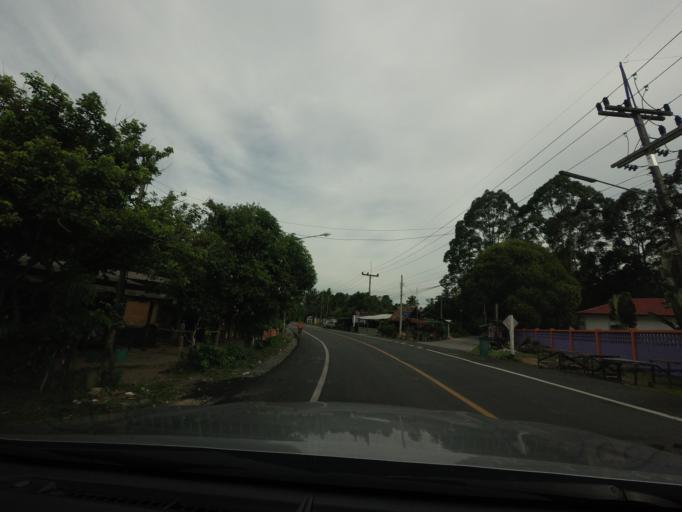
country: TH
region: Yala
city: Raman
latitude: 6.4431
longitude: 101.4513
